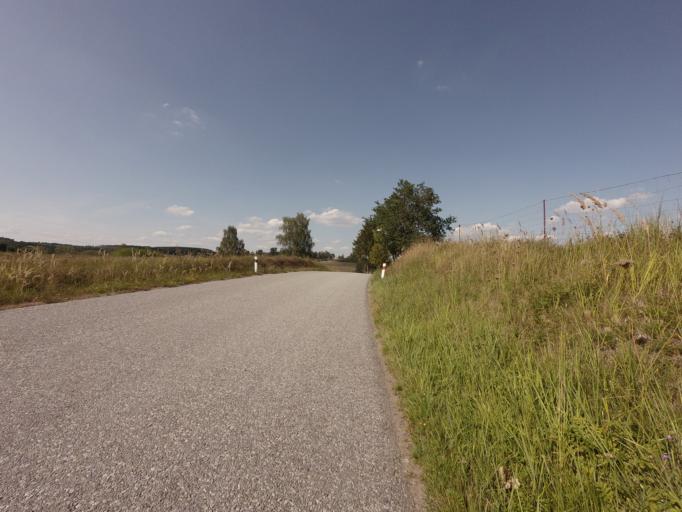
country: CZ
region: Jihocesky
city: Tyn nad Vltavou
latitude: 49.1683
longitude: 14.4251
